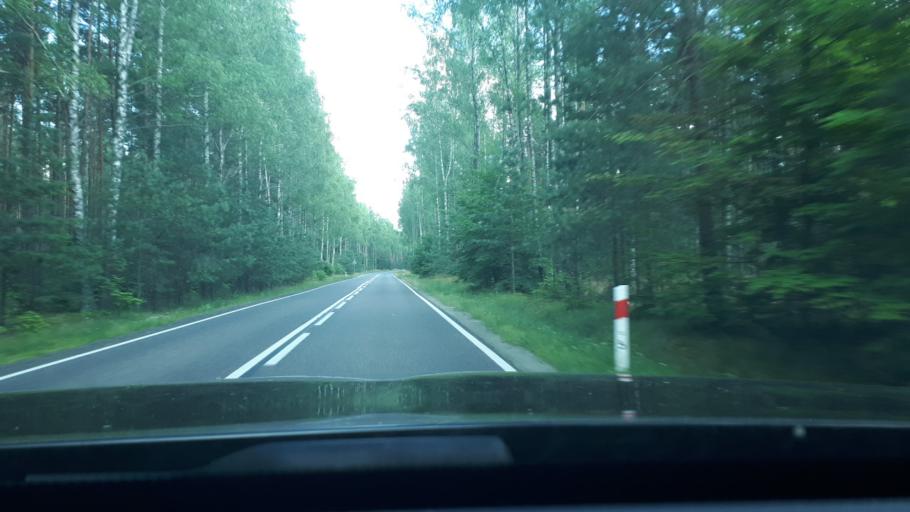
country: PL
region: Warmian-Masurian Voivodeship
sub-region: Powiat olsztynski
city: Stawiguda
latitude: 53.5336
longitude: 20.4342
